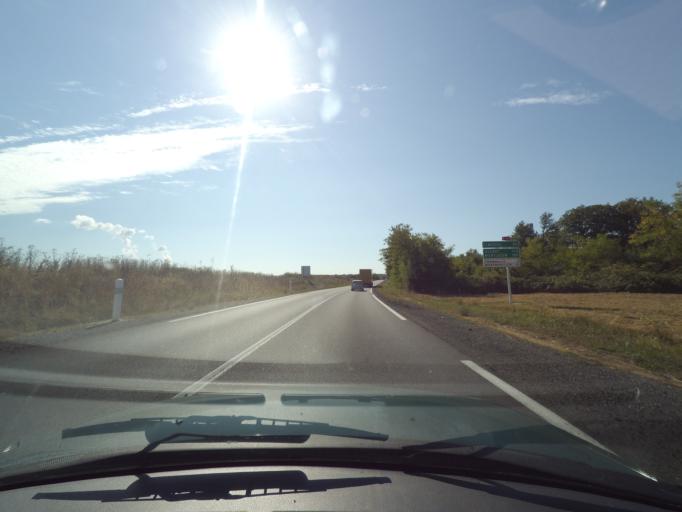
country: FR
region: Poitou-Charentes
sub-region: Departement de la Vienne
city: Terce
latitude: 46.4545
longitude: 0.5608
